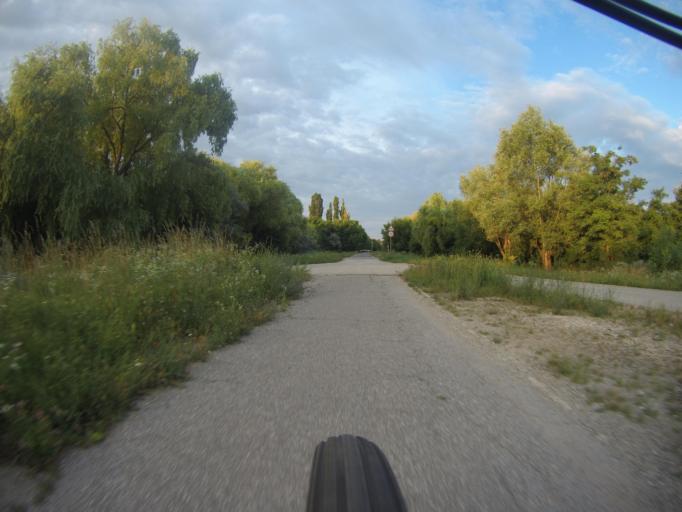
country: HU
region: Pest
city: Budakalasz
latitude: 47.6125
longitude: 19.0759
